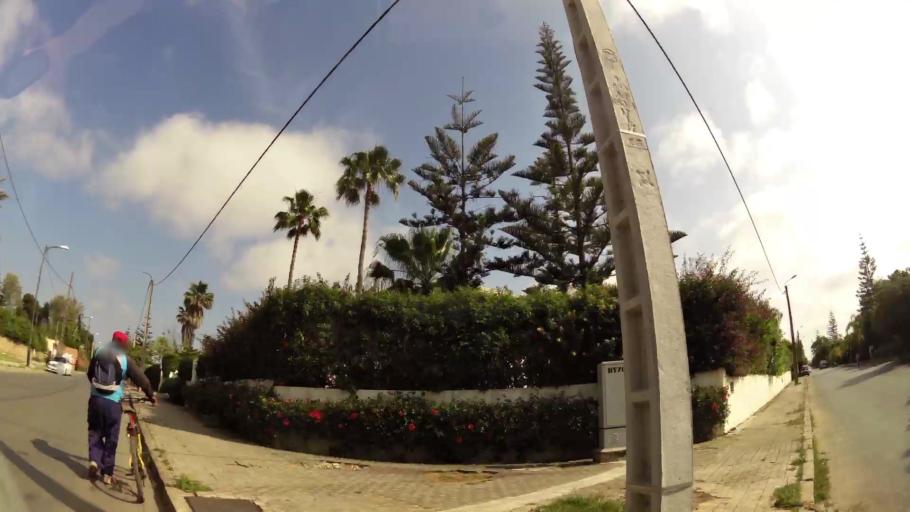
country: MA
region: Rabat-Sale-Zemmour-Zaer
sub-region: Rabat
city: Rabat
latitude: 33.9692
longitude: -6.8557
